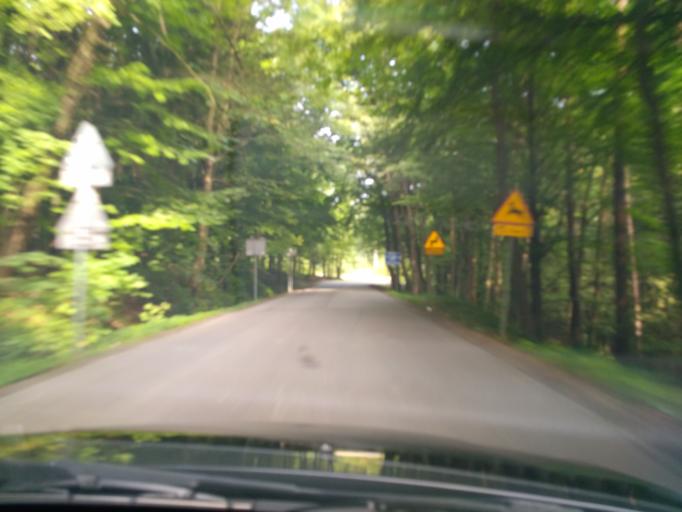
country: PL
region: Subcarpathian Voivodeship
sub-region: Powiat strzyzowski
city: Czudec
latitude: 49.9660
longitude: 21.8406
